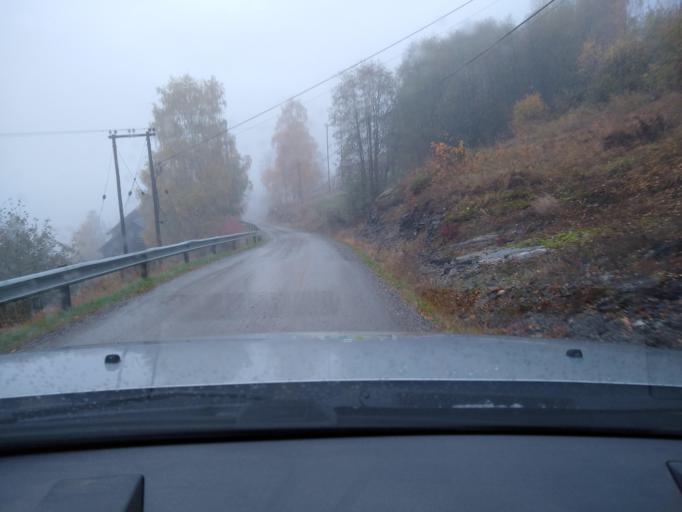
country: NO
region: Oppland
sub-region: Ringebu
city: Ringebu
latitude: 61.5262
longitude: 10.1613
